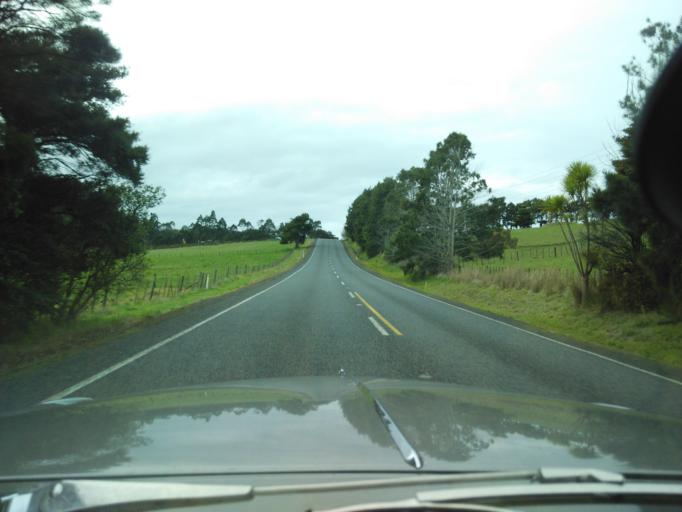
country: NZ
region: Auckland
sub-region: Auckland
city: Parakai
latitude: -36.6303
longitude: 174.5545
